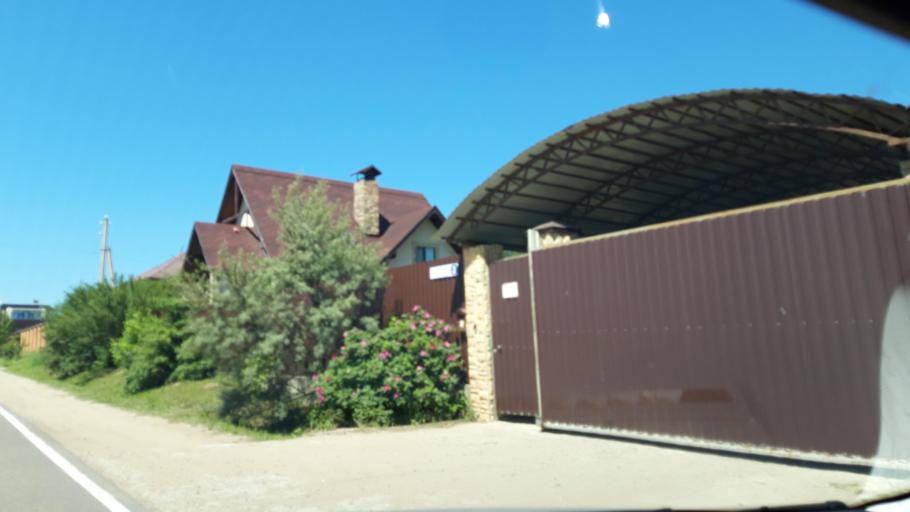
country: RU
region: Moskovskaya
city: Solnechnogorsk
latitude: 56.1656
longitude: 36.9699
